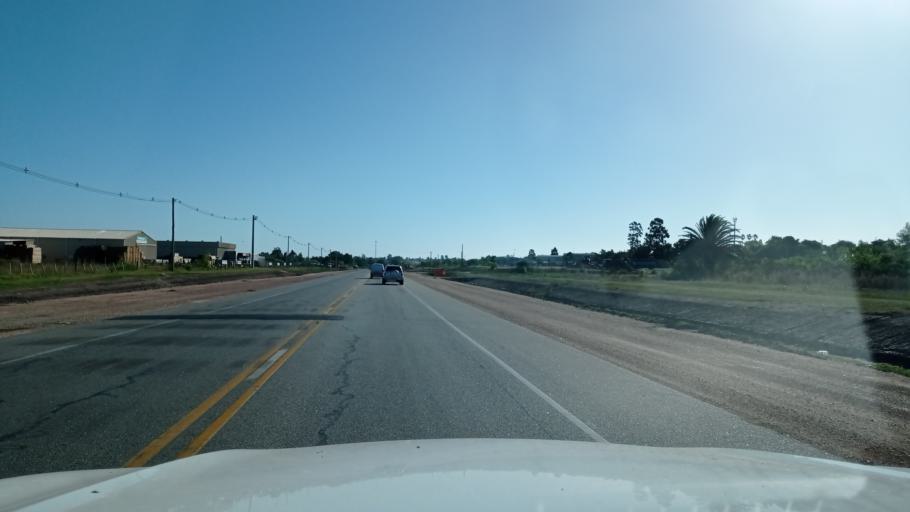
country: UY
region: Canelones
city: Pando
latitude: -34.7263
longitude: -55.9505
